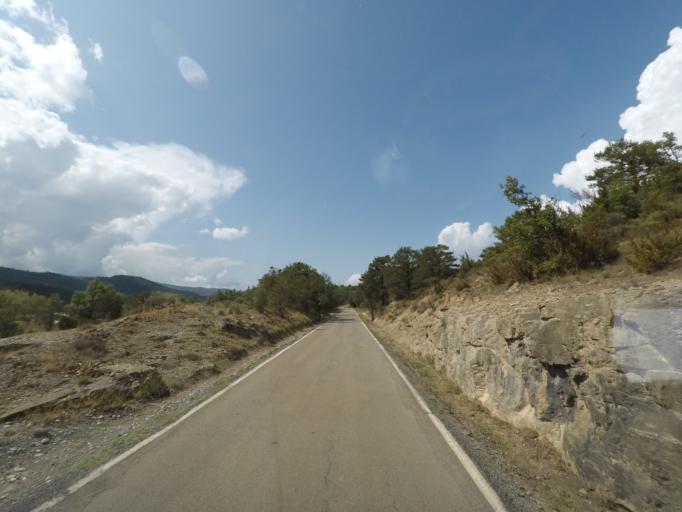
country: ES
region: Aragon
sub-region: Provincia de Huesca
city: Yebra de Basa
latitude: 42.3983
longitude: -0.3308
